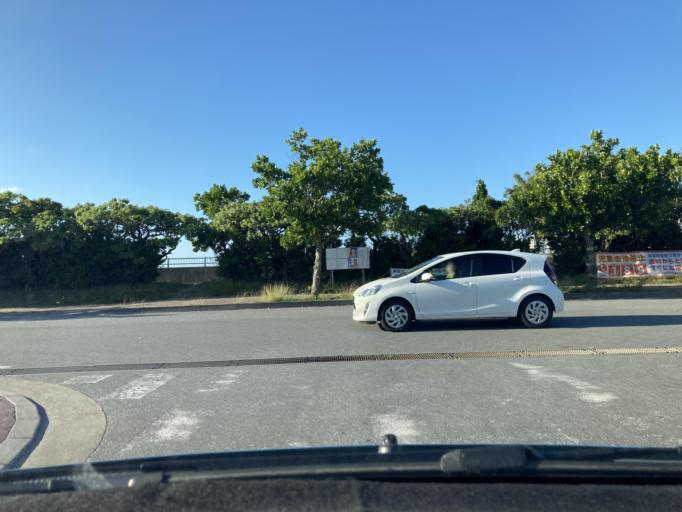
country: JP
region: Okinawa
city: Itoman
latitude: 26.1242
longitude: 127.6657
